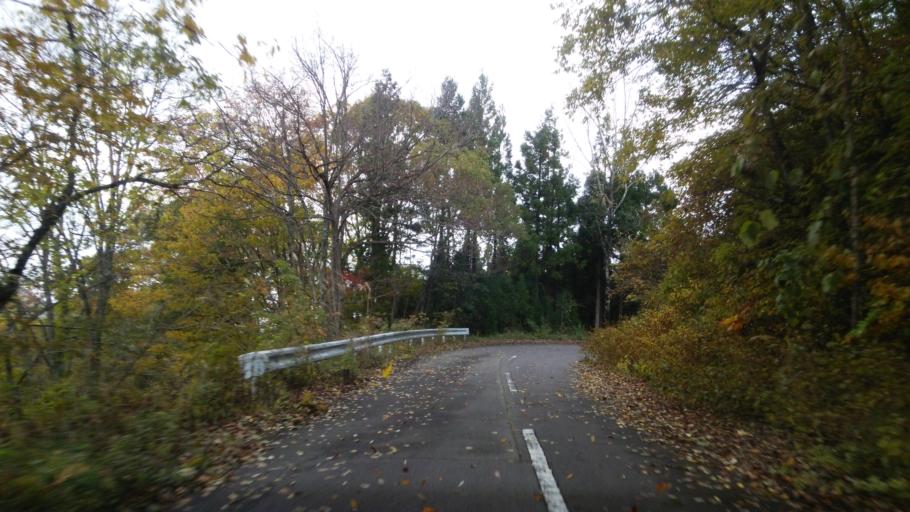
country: JP
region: Fukushima
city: Kitakata
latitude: 37.3925
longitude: 139.7388
